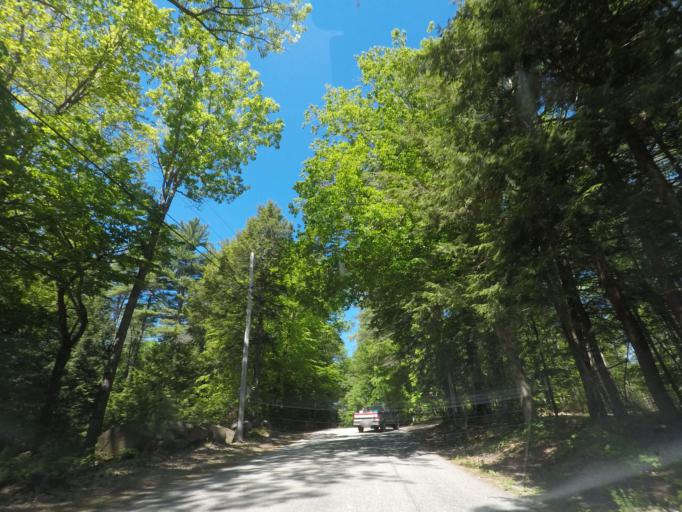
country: US
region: Maine
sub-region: Kennebec County
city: Winthrop
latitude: 44.2649
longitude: -69.9197
